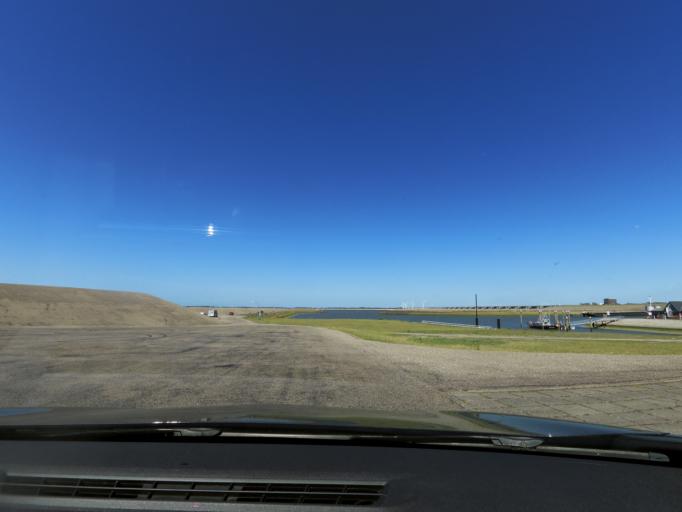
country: NL
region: South Holland
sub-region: Gemeente Goeree-Overflakkee
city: Goedereede
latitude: 51.8267
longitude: 4.0276
